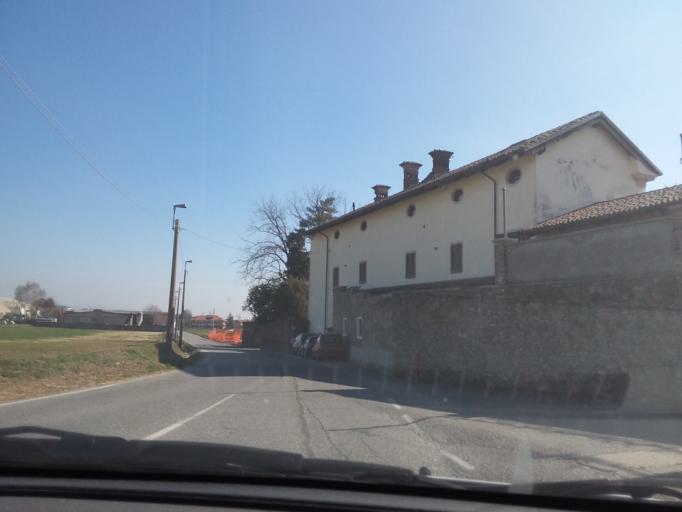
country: IT
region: Piedmont
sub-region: Provincia di Torino
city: Tetti Neirotti
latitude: 45.0538
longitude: 7.5375
